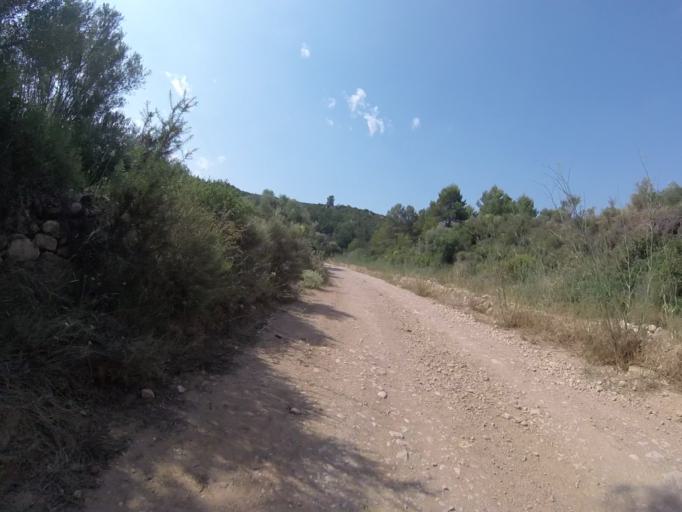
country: ES
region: Valencia
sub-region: Provincia de Castello
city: Cuevas de Vinroma
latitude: 40.3044
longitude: 0.1700
